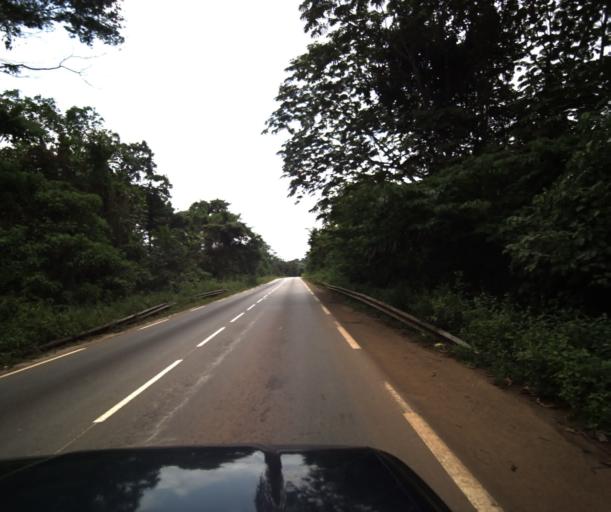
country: CM
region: Centre
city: Eseka
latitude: 3.8774
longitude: 10.8382
